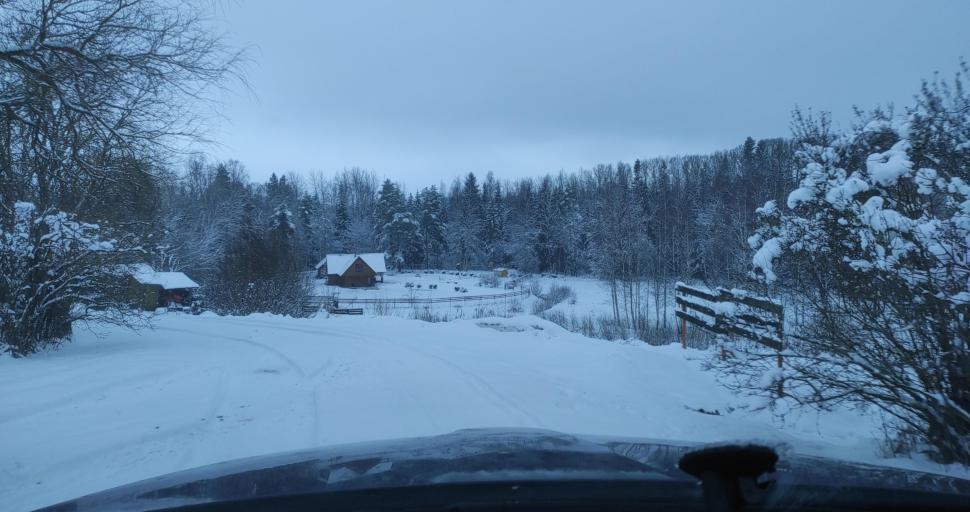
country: LV
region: Kuldigas Rajons
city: Kuldiga
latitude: 56.9906
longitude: 22.0442
